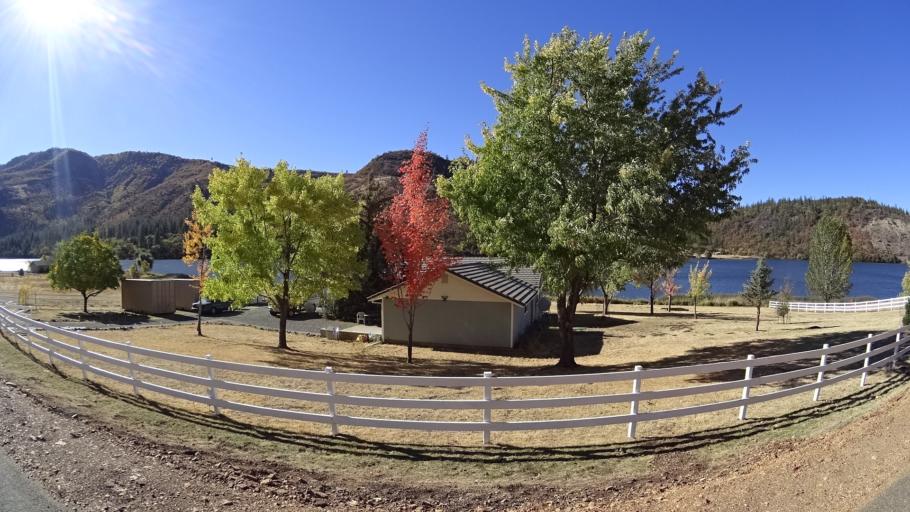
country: US
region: California
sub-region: Siskiyou County
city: Montague
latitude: 41.9718
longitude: -122.2760
